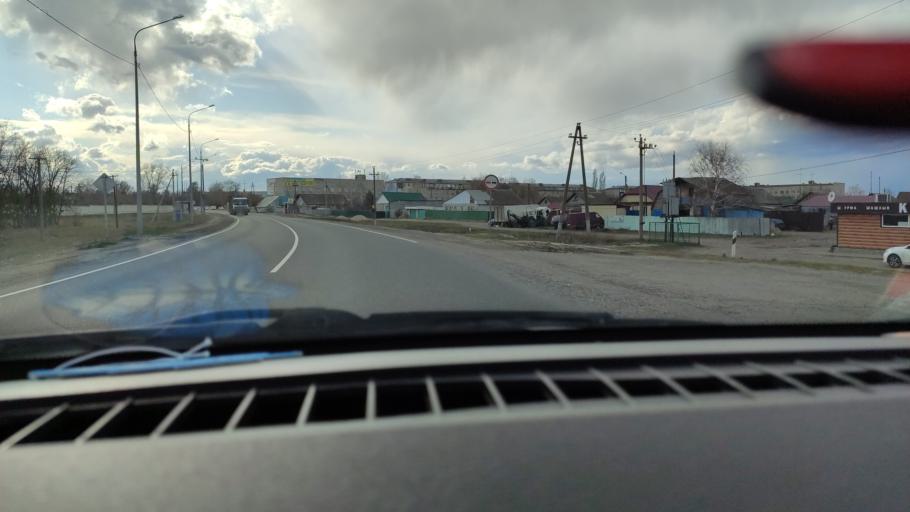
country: RU
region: Saratov
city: Sennoy
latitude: 52.1521
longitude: 46.9604
